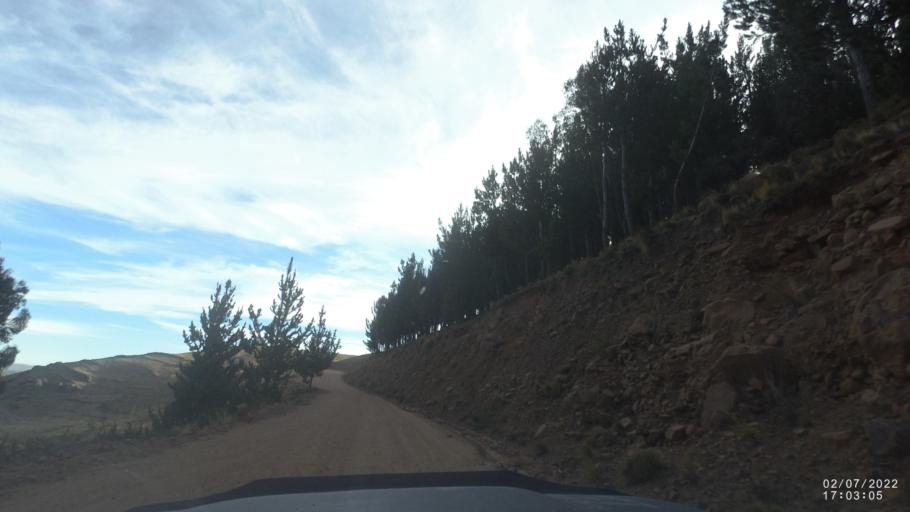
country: BO
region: Cochabamba
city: Irpa Irpa
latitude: -17.9222
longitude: -66.5541
